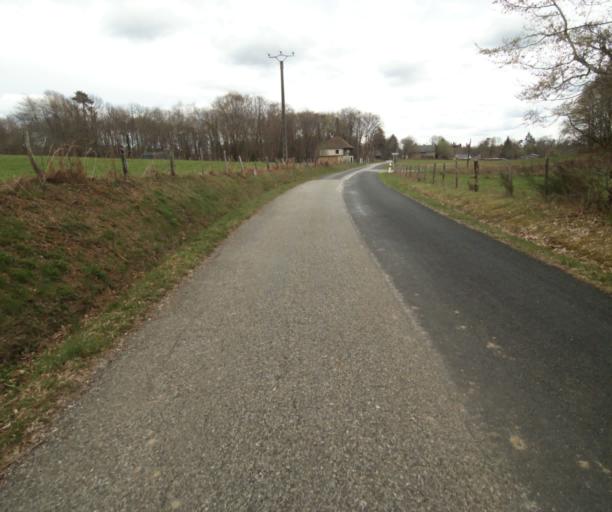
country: FR
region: Limousin
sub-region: Departement de la Correze
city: Argentat
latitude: 45.2116
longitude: 1.9225
